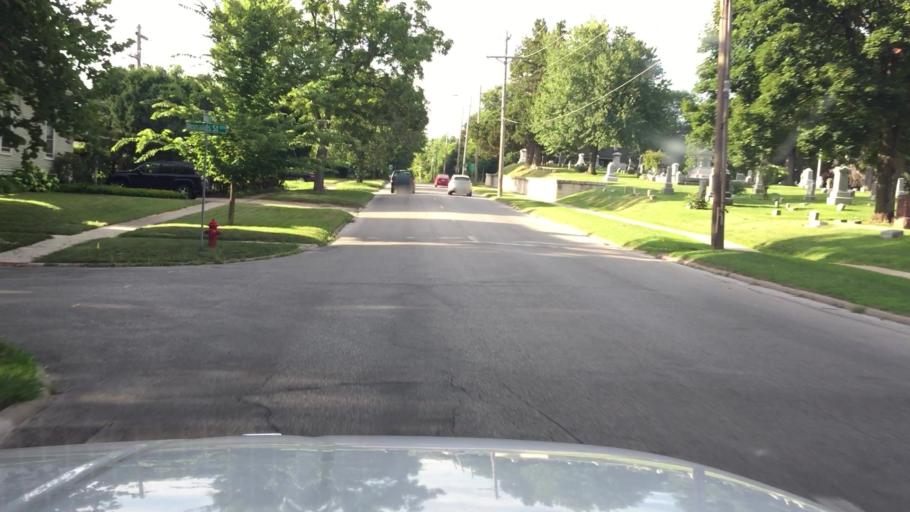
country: US
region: Iowa
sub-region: Johnson County
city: Iowa City
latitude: 41.6689
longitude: -91.5228
